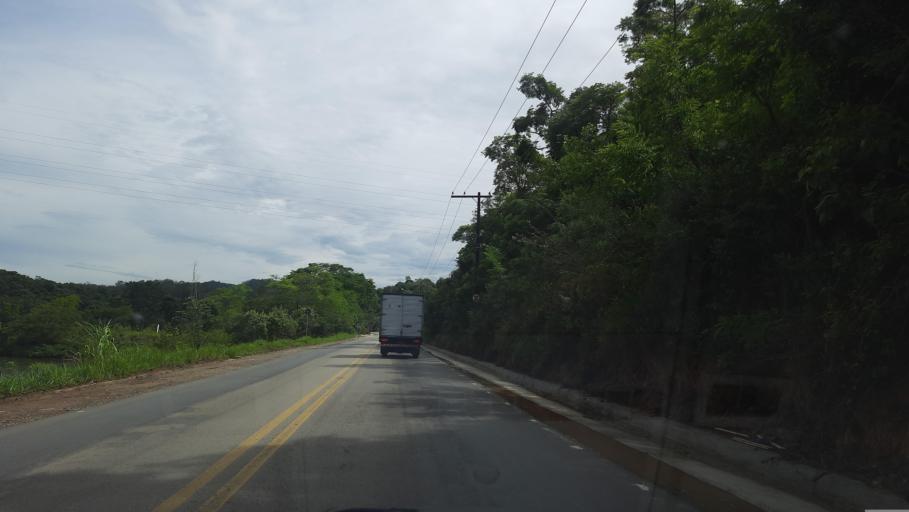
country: BR
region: Sao Paulo
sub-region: Franco Da Rocha
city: Franco da Rocha
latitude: -23.3530
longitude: -46.6646
